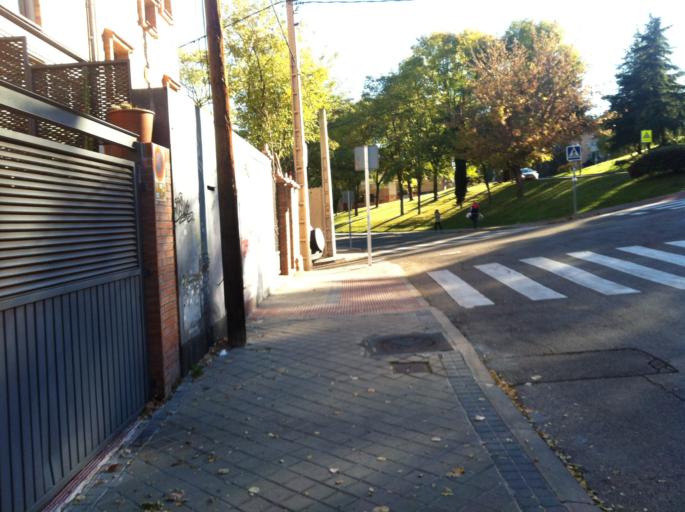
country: ES
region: Madrid
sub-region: Provincia de Madrid
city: Tetuan de las Victorias
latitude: 40.4650
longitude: -3.7150
